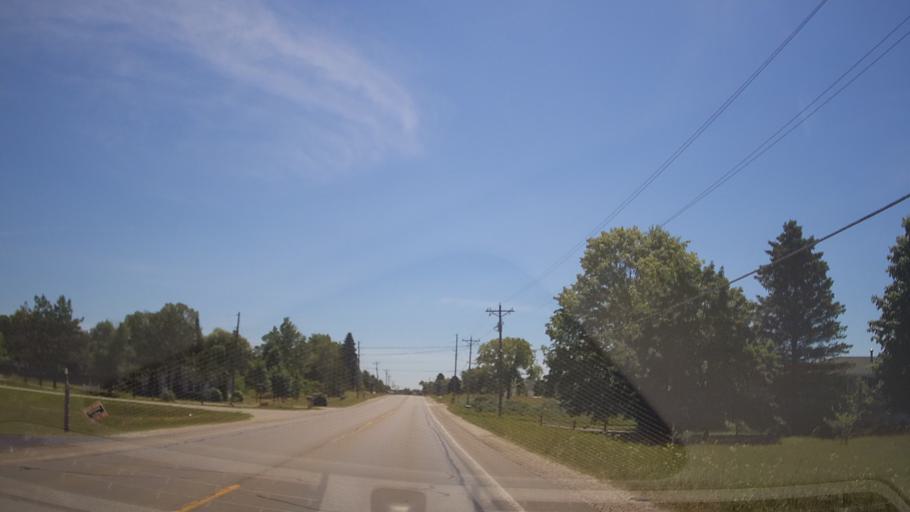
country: US
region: Michigan
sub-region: Grand Traverse County
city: Traverse City
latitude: 44.6715
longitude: -85.6900
